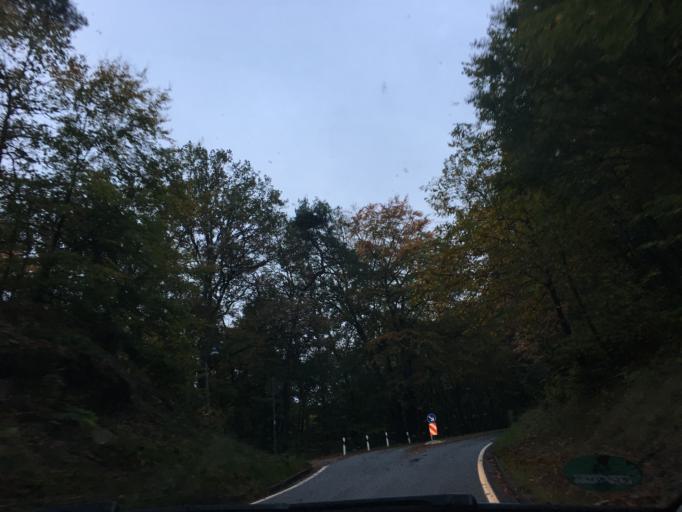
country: DE
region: Rheinland-Pfalz
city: Krickenbach
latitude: 49.3605
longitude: 7.6643
